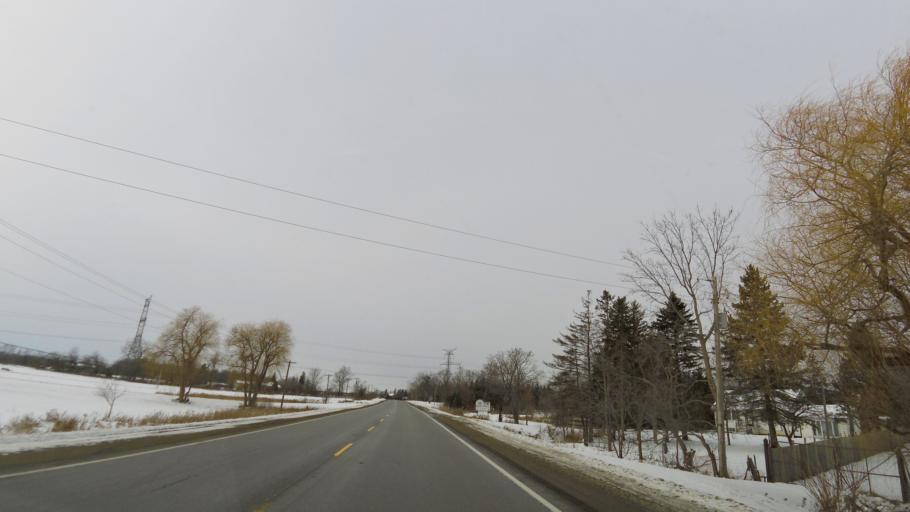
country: CA
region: Ontario
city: Ancaster
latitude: 43.2858
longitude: -80.0812
